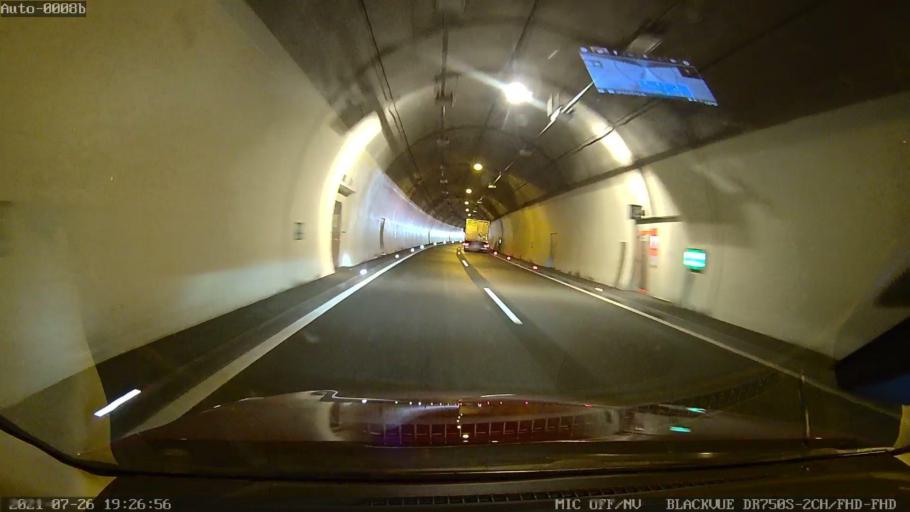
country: AT
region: Upper Austria
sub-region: Politischer Bezirk Kirchdorf an der Krems
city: Micheldorf in Oberoesterreich
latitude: 47.8475
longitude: 14.1672
